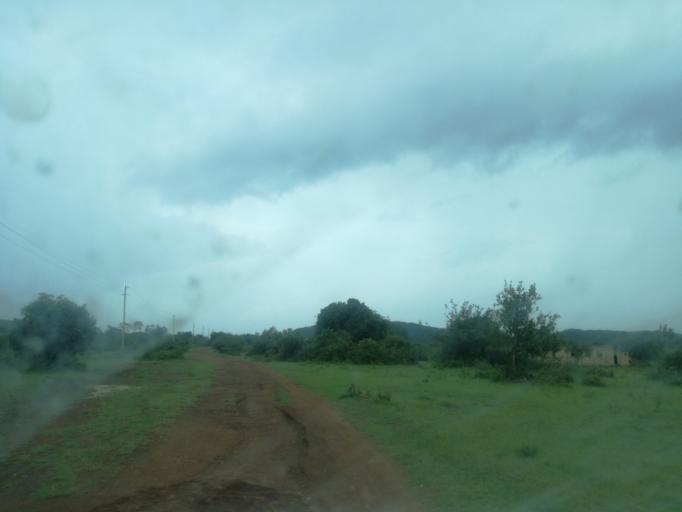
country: TZ
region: Mara
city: Mugumu
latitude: -1.8323
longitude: 34.5732
